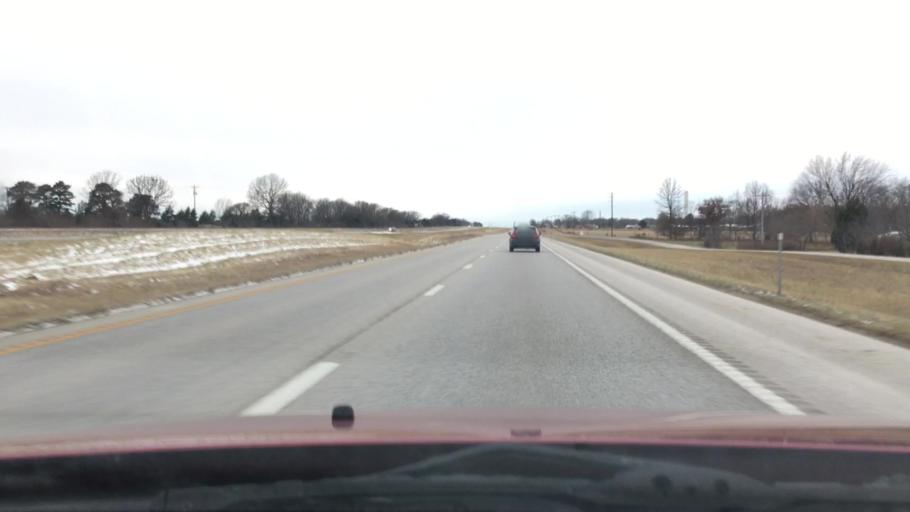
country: US
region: Missouri
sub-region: Webster County
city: Seymour
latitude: 37.1704
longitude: -92.8331
